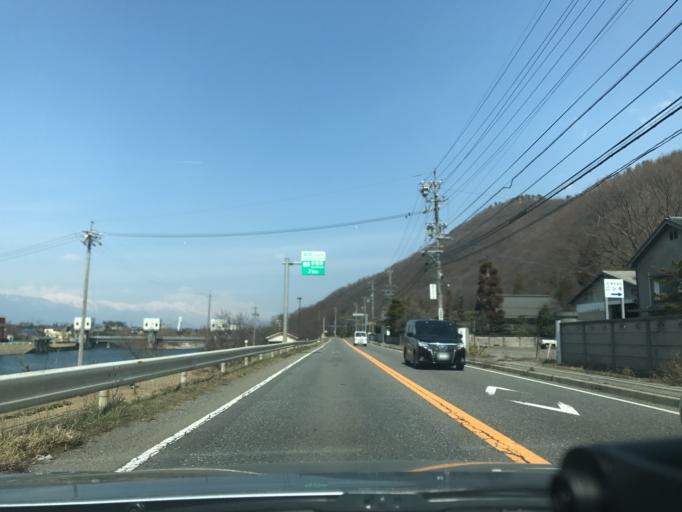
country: JP
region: Nagano
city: Matsumoto
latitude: 36.2515
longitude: 137.9514
